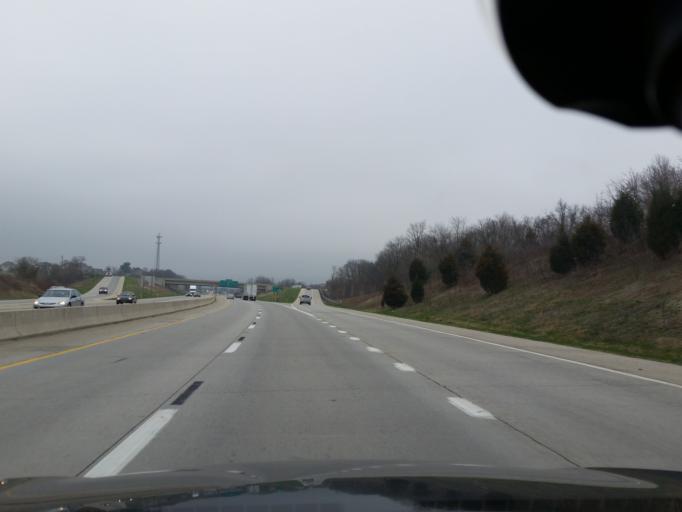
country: US
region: Pennsylvania
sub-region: Cumberland County
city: Mechanicsburg
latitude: 40.2551
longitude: -76.9893
